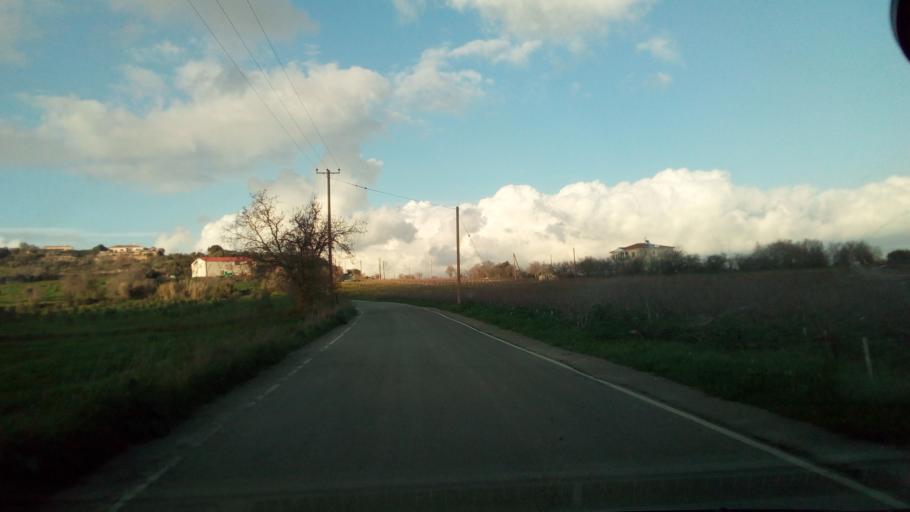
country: CY
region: Pafos
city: Mesogi
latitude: 34.8715
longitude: 32.5052
